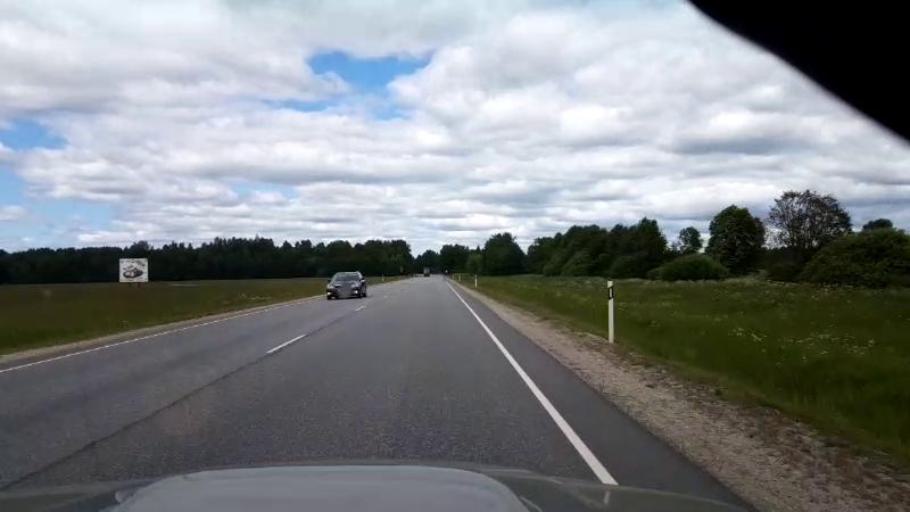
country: EE
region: Raplamaa
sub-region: Maerjamaa vald
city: Marjamaa
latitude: 58.9429
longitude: 24.4670
